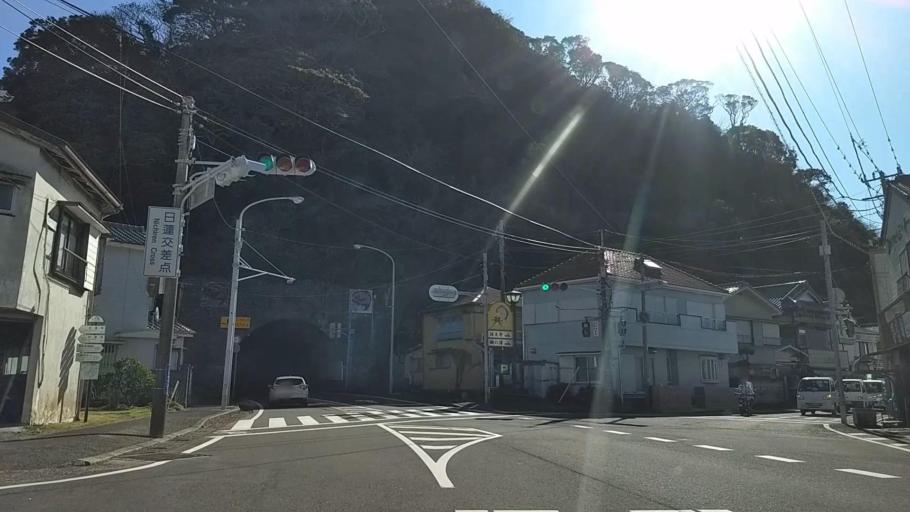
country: JP
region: Chiba
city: Kawaguchi
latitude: 35.1224
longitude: 140.1985
